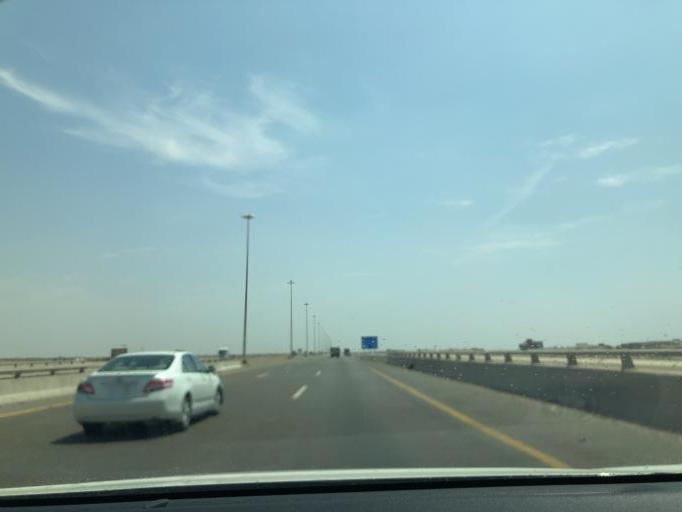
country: SA
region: Makkah
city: Rabigh
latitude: 22.2676
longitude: 39.1226
